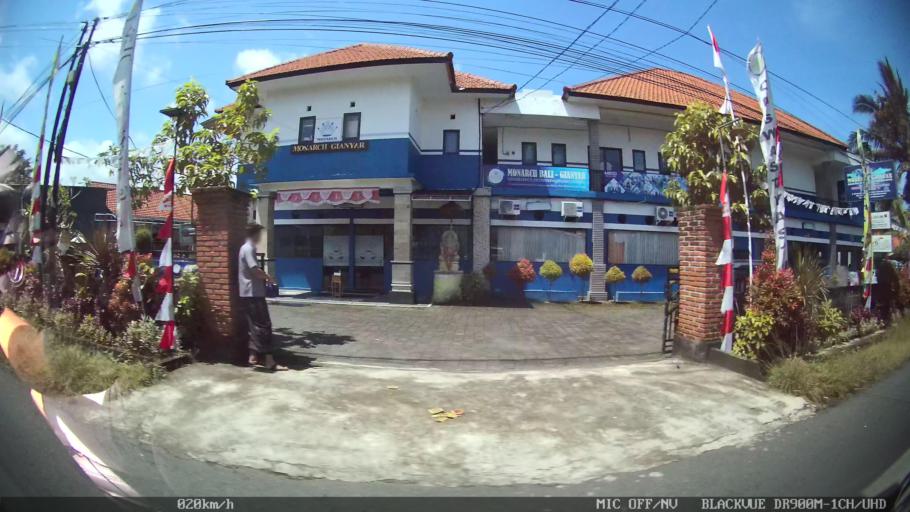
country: ID
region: Bali
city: Banjar Kelodan
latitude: -8.5355
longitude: 115.3345
